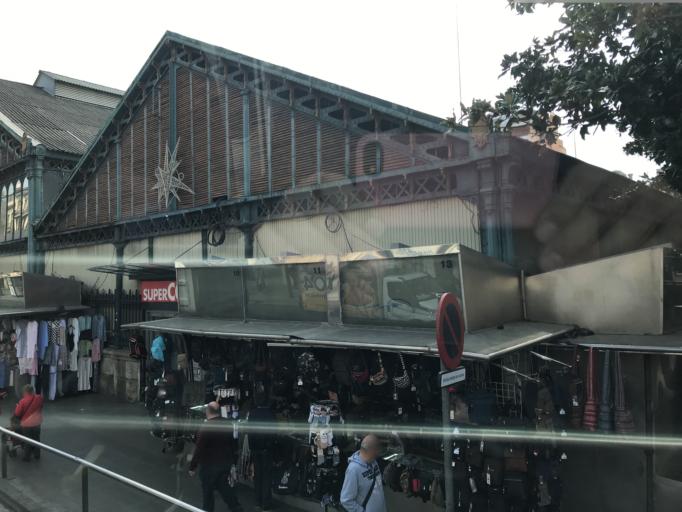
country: ES
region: Catalonia
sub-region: Provincia de Barcelona
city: Sants-Montjuic
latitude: 41.3753
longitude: 2.1434
